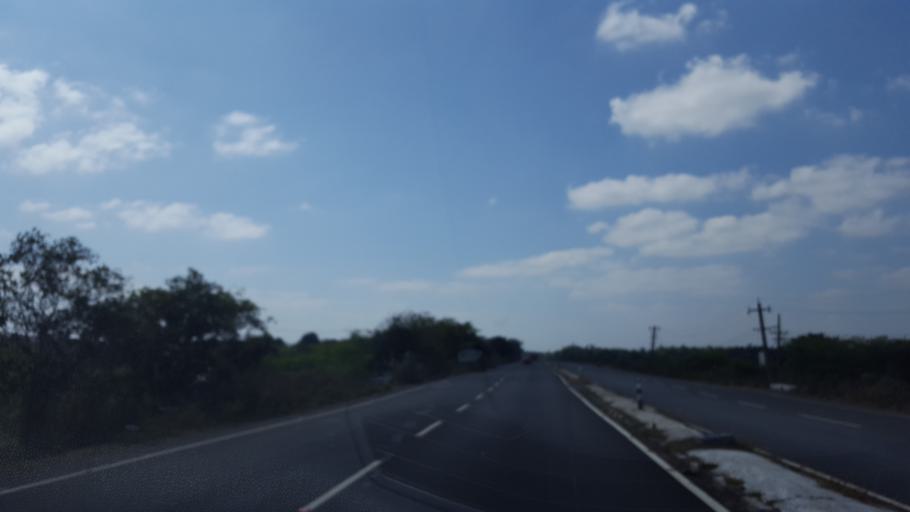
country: IN
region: Tamil Nadu
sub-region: Kancheepuram
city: Mamallapuram
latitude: 12.6606
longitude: 80.1771
